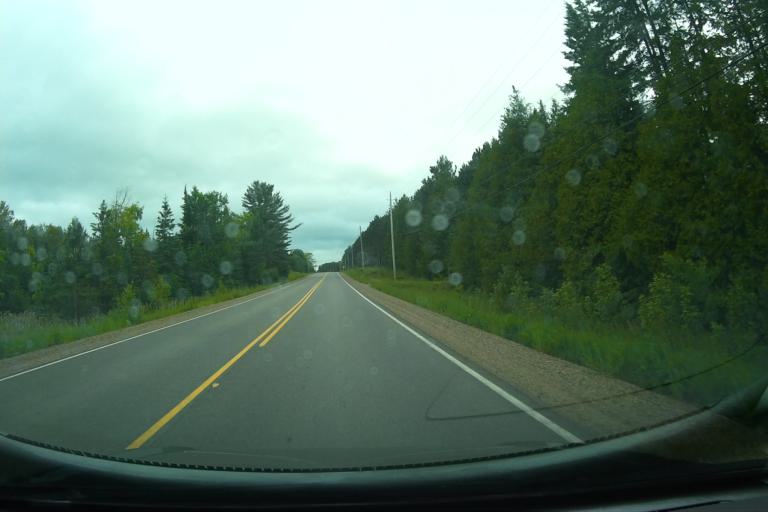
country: CA
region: Ontario
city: Pembroke
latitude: 45.5201
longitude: -77.1173
